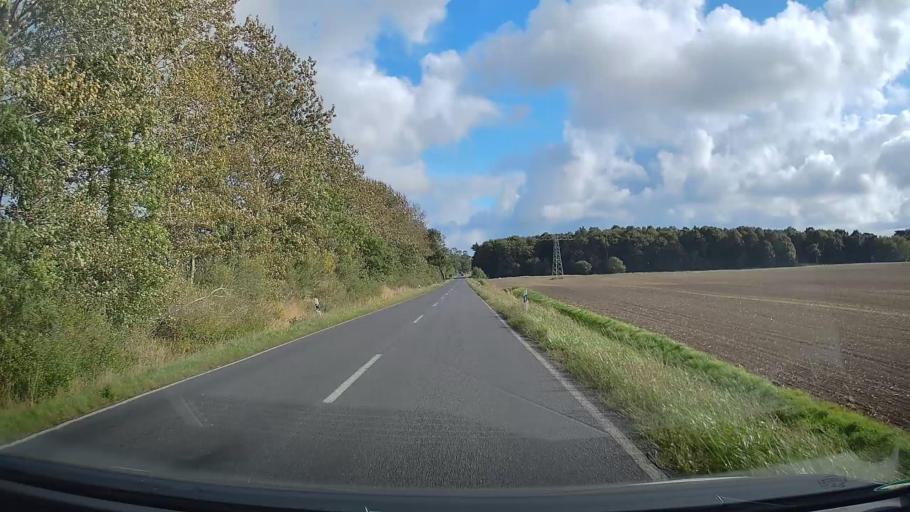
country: DE
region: Mecklenburg-Vorpommern
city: Bergen auf Ruegen
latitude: 54.4011
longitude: 13.4548
